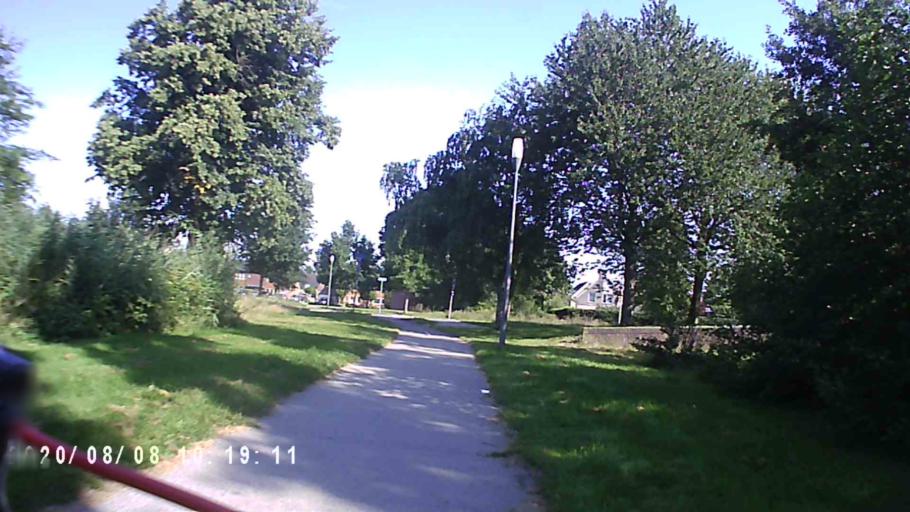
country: NL
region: Groningen
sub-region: Gemeente Leek
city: Leek
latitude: 53.1359
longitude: 6.4008
